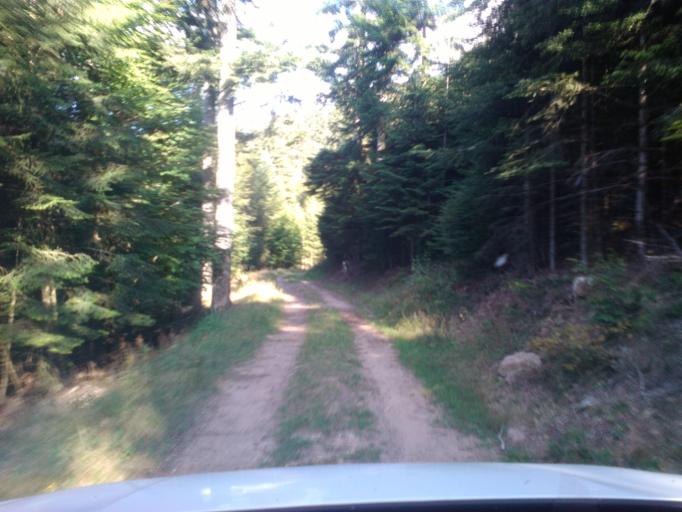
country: FR
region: Lorraine
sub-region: Departement des Vosges
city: Senones
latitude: 48.4275
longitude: 7.0401
